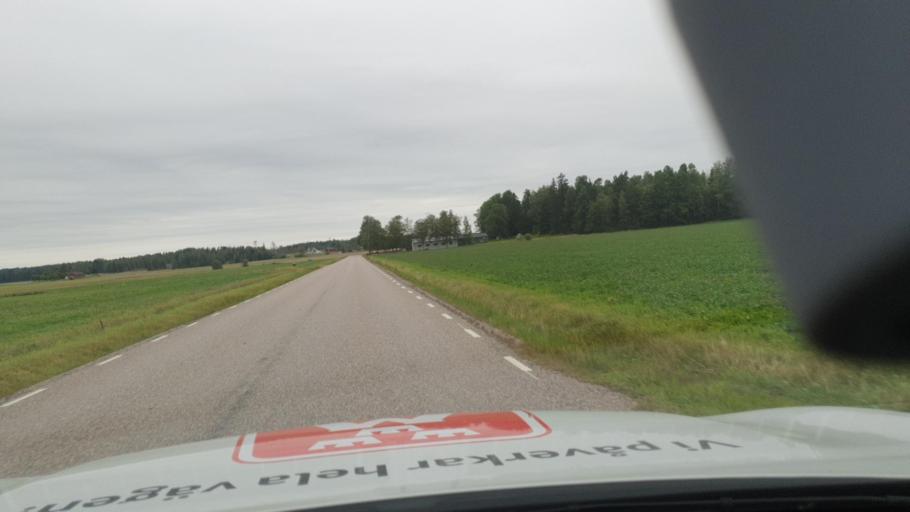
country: SE
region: Vaestra Goetaland
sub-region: Vanersborgs Kommun
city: Vanersborg
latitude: 58.4979
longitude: 12.1829
